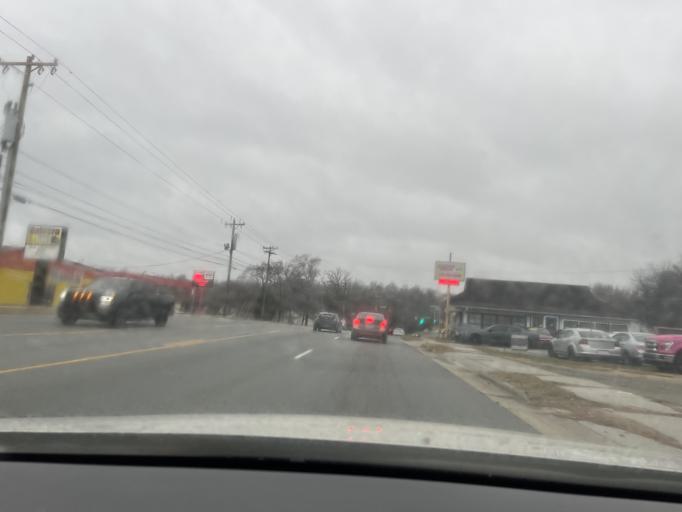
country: US
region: North Carolina
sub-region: Guilford County
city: Greensboro
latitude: 36.0253
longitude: -79.8025
